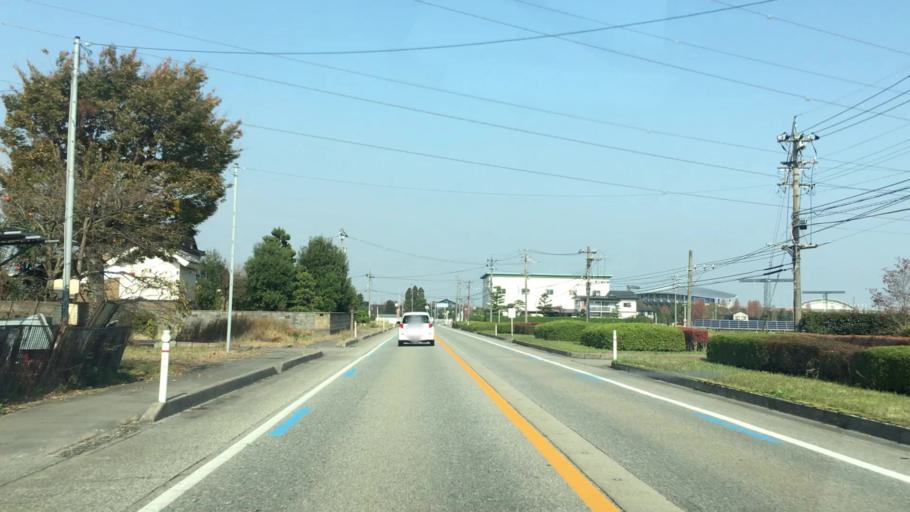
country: JP
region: Toyama
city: Toyama-shi
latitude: 36.6194
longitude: 137.1930
